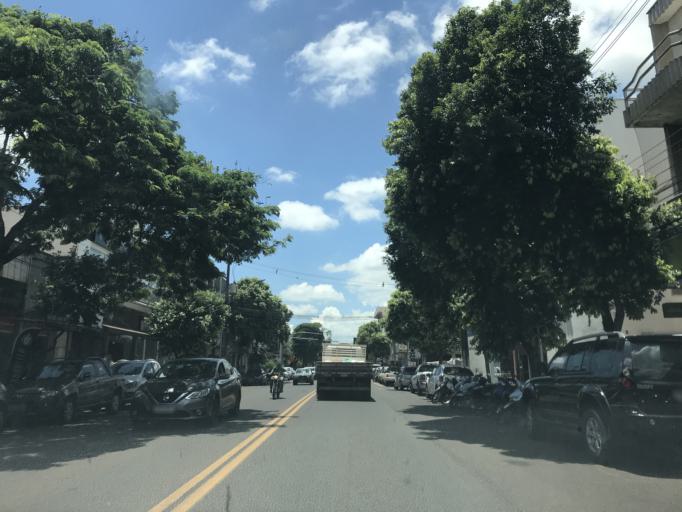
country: BR
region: Parana
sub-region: Marialva
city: Marialva
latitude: -23.4867
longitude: -51.7964
